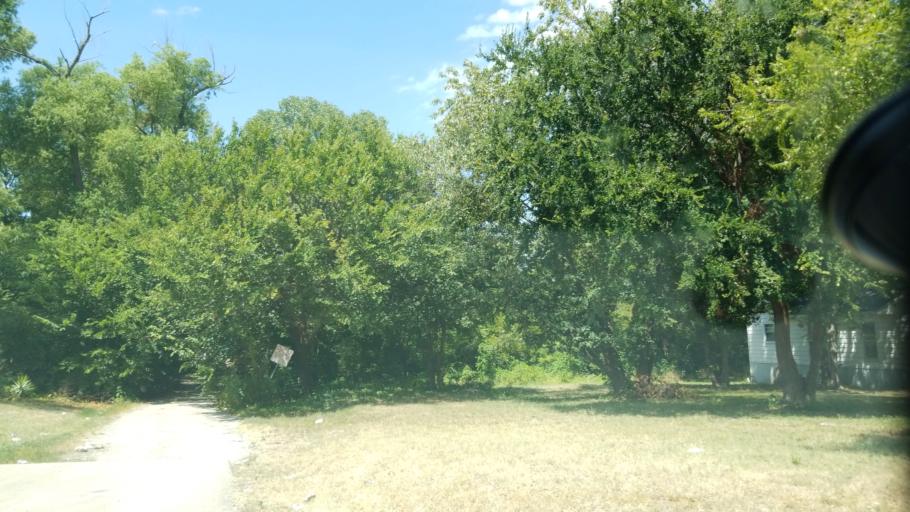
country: US
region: Texas
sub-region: Dallas County
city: Cockrell Hill
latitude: 32.7313
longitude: -96.8978
